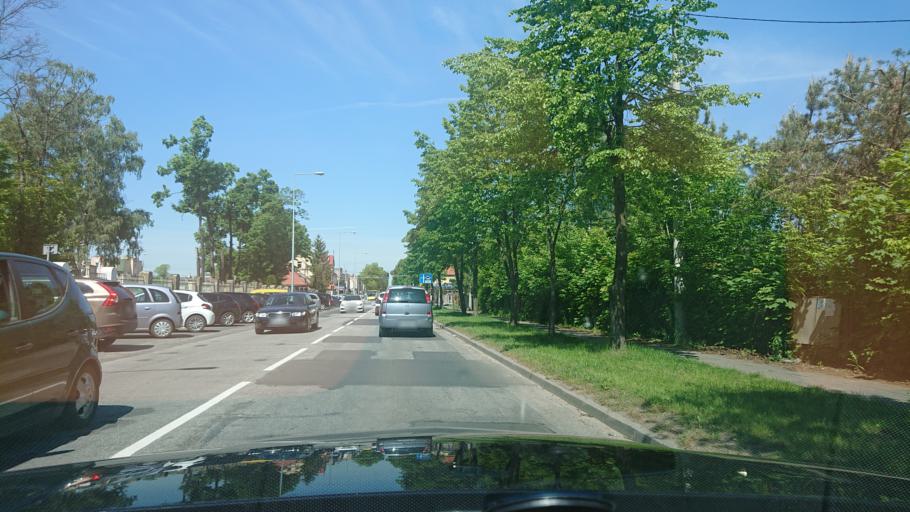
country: PL
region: Greater Poland Voivodeship
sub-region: Powiat gnieznienski
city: Gniezno
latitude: 52.5195
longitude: 17.6069
